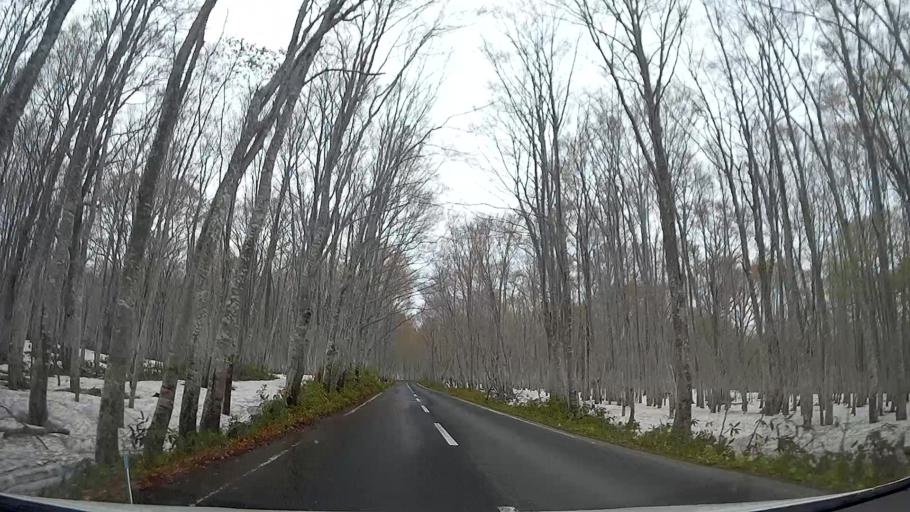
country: JP
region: Aomori
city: Aomori Shi
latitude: 40.6297
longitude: 140.9352
